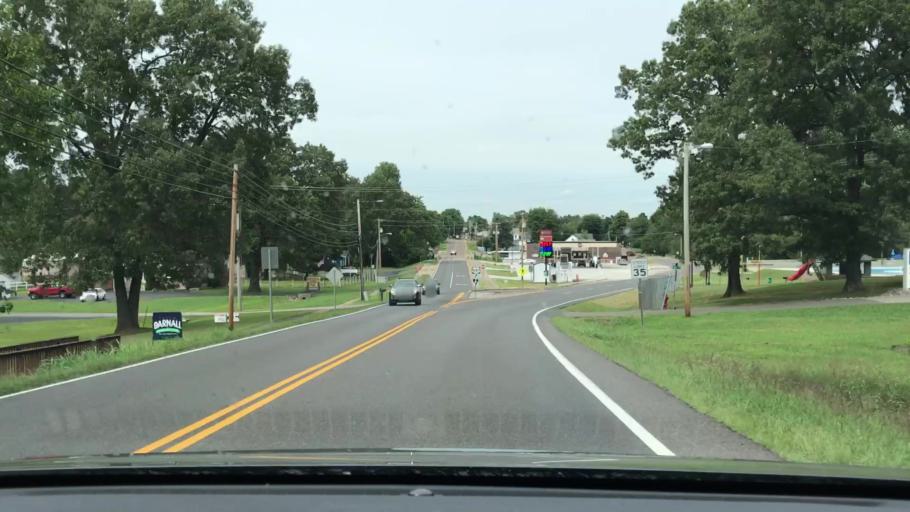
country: US
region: Kentucky
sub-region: Marshall County
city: Benton
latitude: 36.8499
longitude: -88.3503
